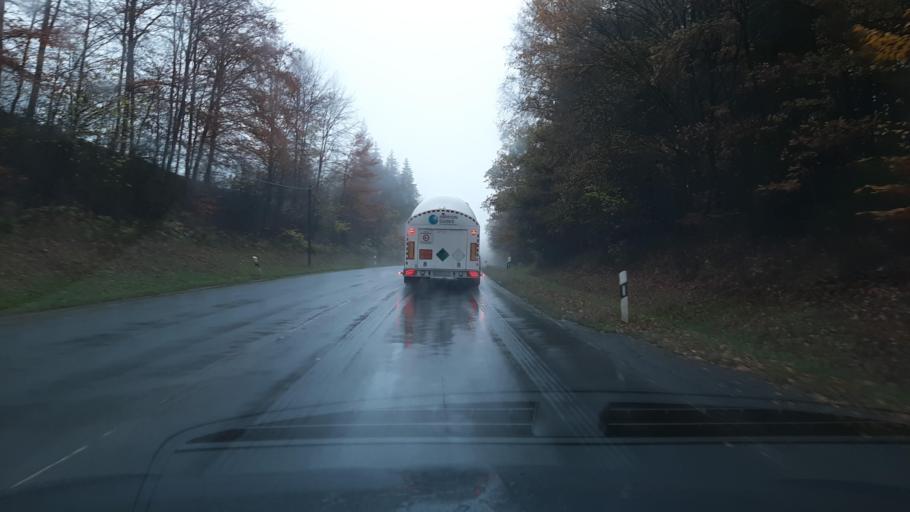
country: DE
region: North Rhine-Westphalia
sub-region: Regierungsbezirk Arnsberg
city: Bad Fredeburg
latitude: 51.2108
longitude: 8.3329
